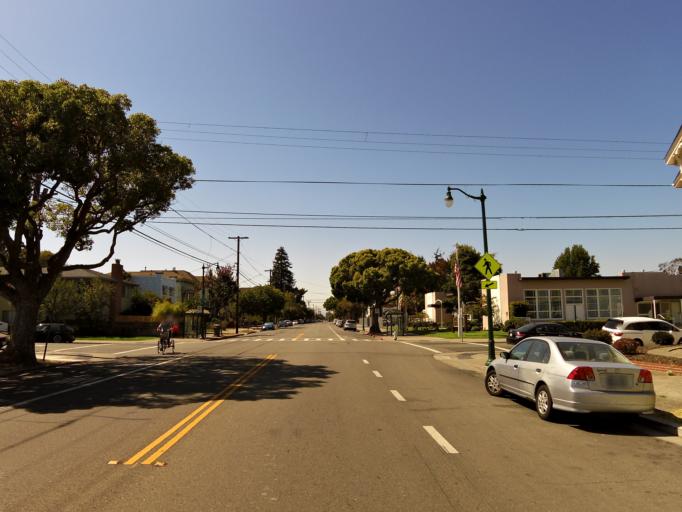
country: US
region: California
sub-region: Alameda County
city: Alameda
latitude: 37.7728
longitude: -122.2645
